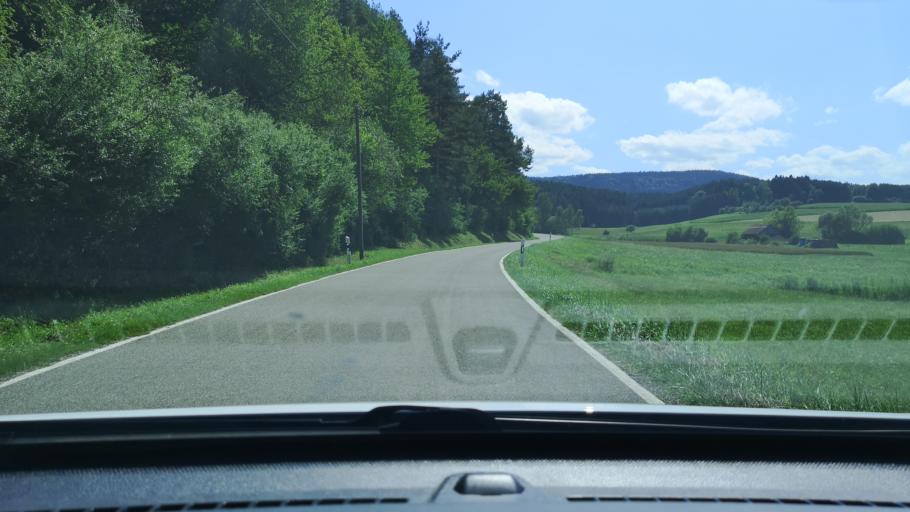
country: DE
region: Baden-Wuerttemberg
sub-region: Freiburg Region
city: Muhlheim am Bach
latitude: 48.3668
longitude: 8.7095
